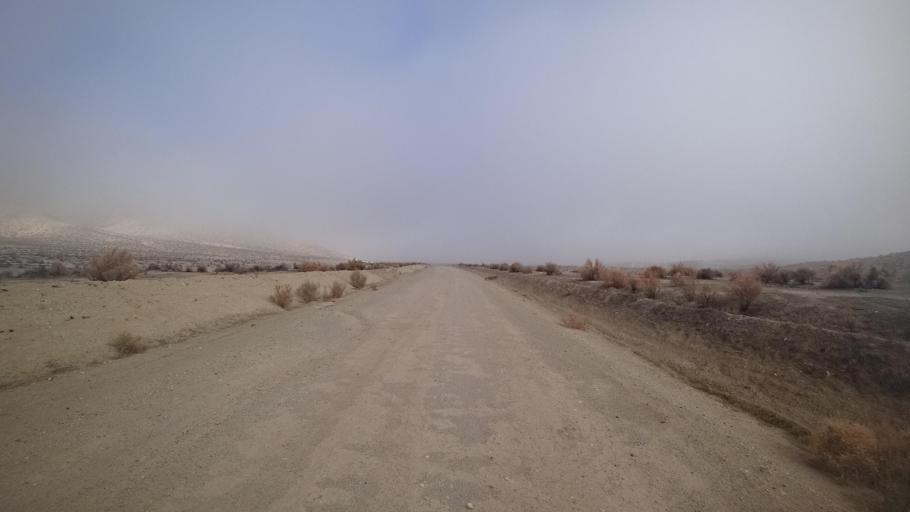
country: US
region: California
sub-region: Kern County
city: Maricopa
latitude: 35.0323
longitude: -119.4396
